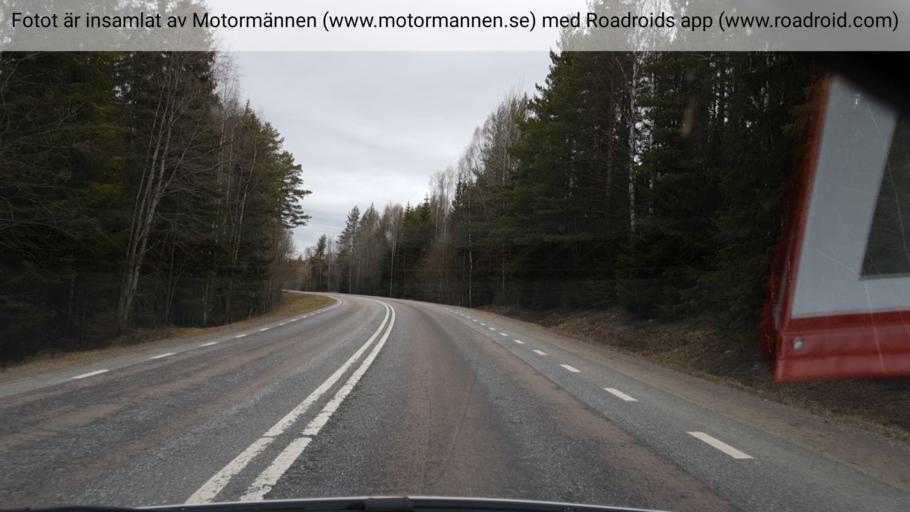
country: SE
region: Vaesternorrland
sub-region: Solleftea Kommun
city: Solleftea
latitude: 63.2876
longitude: 17.2233
